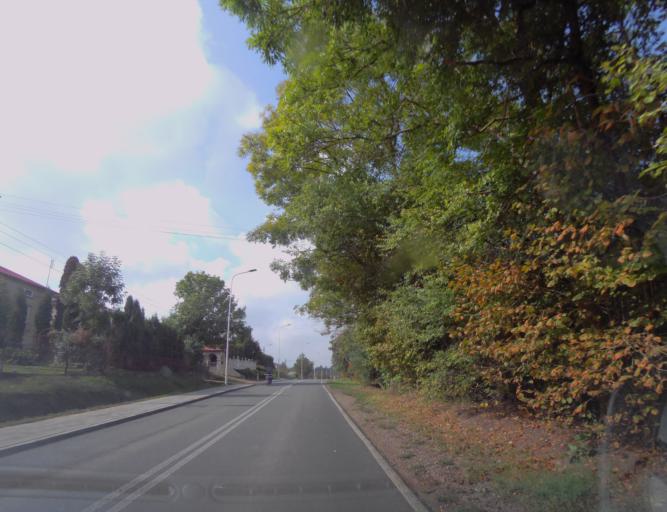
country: PL
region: Lublin Voivodeship
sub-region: Powiat krasnostawski
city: Krasnystaw
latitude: 50.9707
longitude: 23.1572
